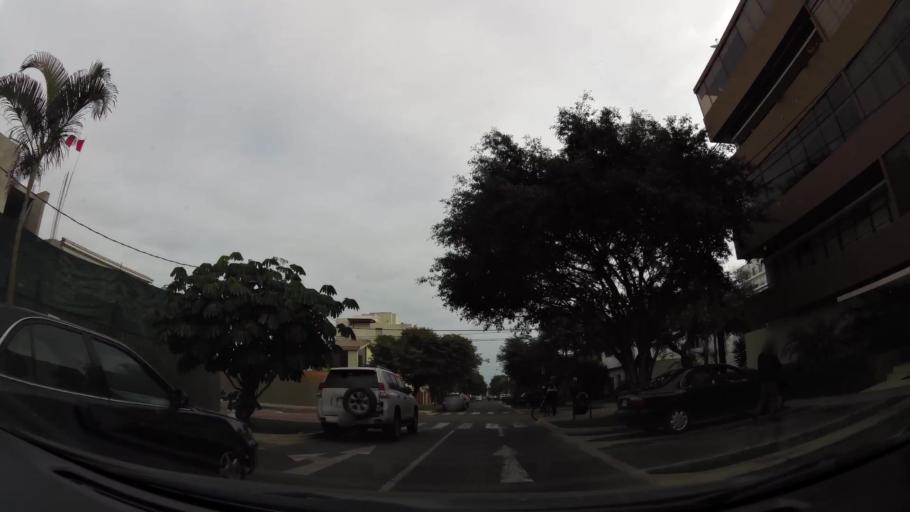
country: PE
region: Lima
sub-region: Lima
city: San Isidro
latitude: -12.1004
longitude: -77.0558
